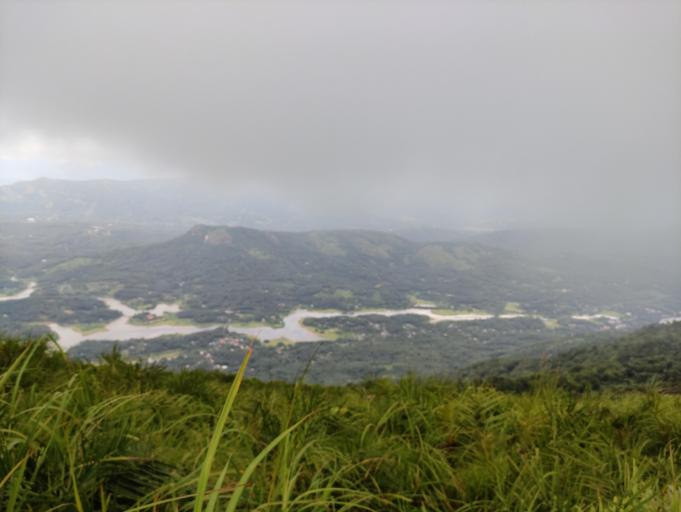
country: IN
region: Kerala
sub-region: Kottayam
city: Erattupetta
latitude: 9.8073
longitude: 76.7806
